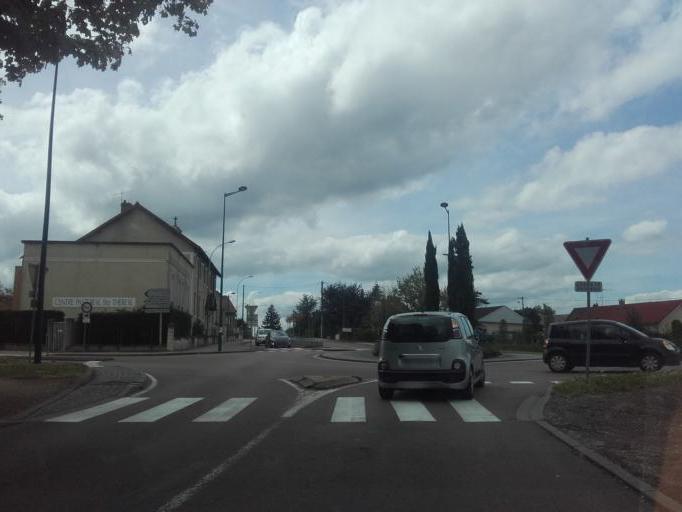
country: FR
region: Bourgogne
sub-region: Departement de Saone-et-Loire
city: Saint-Remy
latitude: 46.7739
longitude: 4.8293
